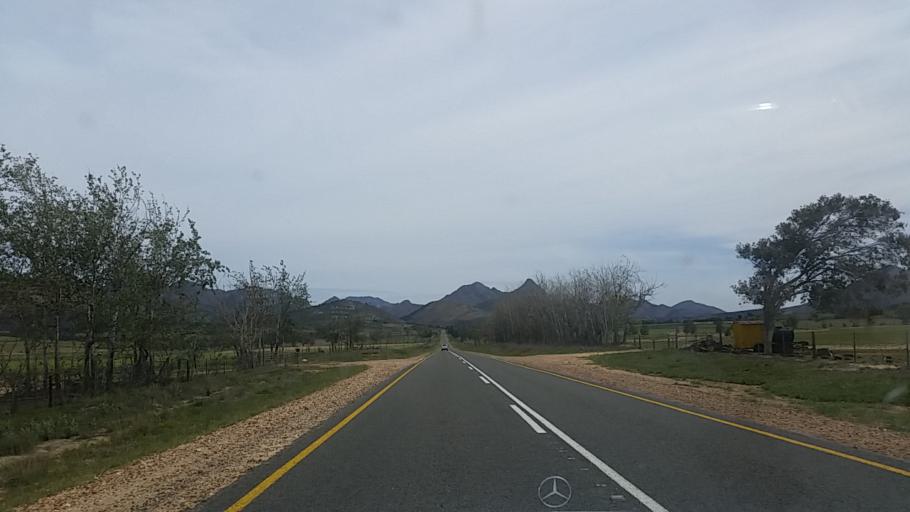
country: ZA
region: Western Cape
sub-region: Eden District Municipality
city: George
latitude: -33.8235
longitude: 22.4845
